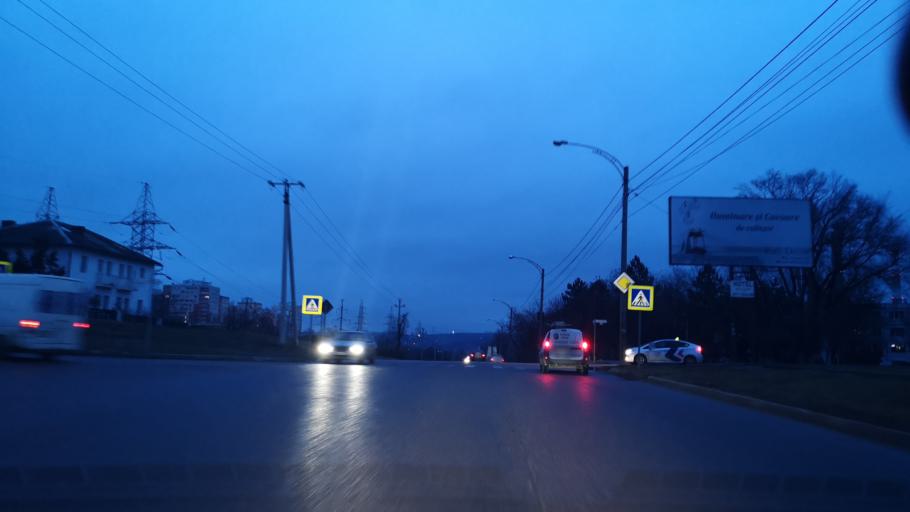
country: MD
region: Chisinau
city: Chisinau
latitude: 47.0296
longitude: 28.8793
